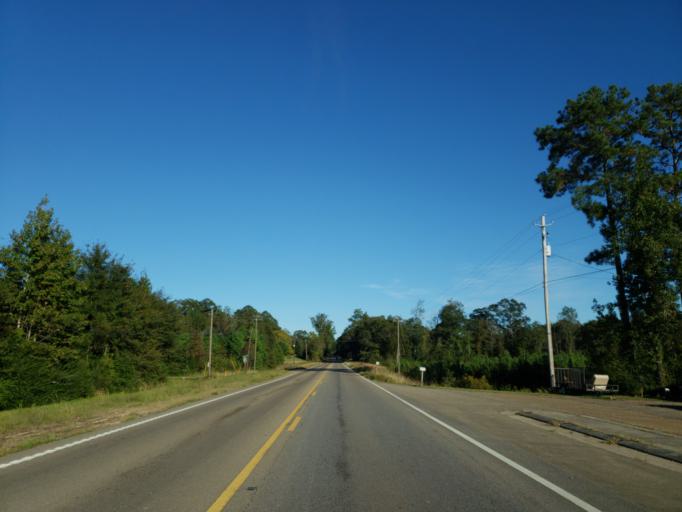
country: US
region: Mississippi
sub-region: Perry County
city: Richton
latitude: 31.3564
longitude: -88.9199
